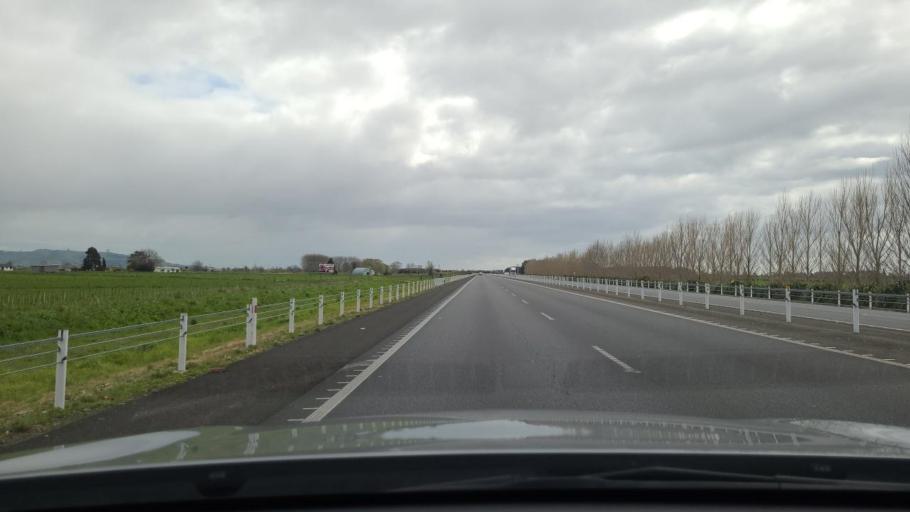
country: NZ
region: Bay of Plenty
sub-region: Western Bay of Plenty District
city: Maketu
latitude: -37.7697
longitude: 176.3766
